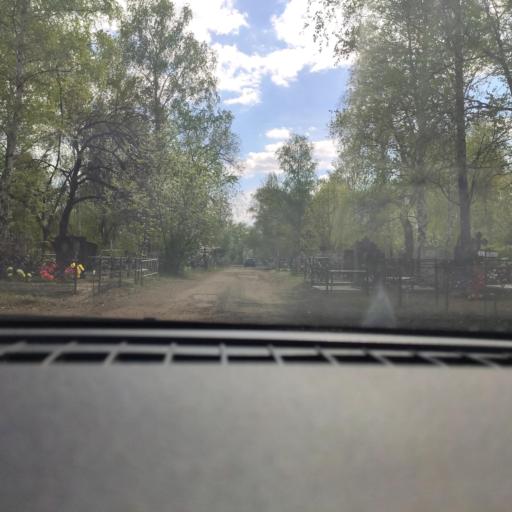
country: RU
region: Voronezj
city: Somovo
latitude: 51.6604
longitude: 39.2971
